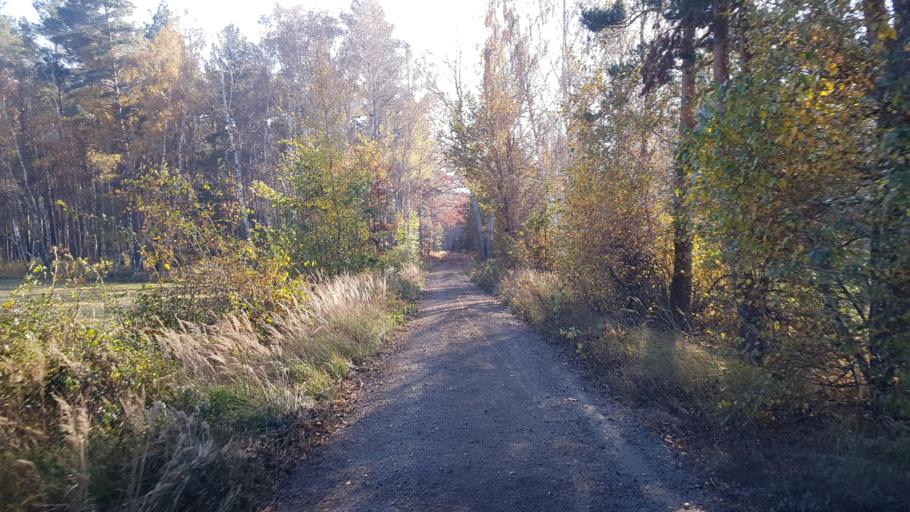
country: DE
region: Brandenburg
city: Ruckersdorf
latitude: 51.5641
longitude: 13.6210
